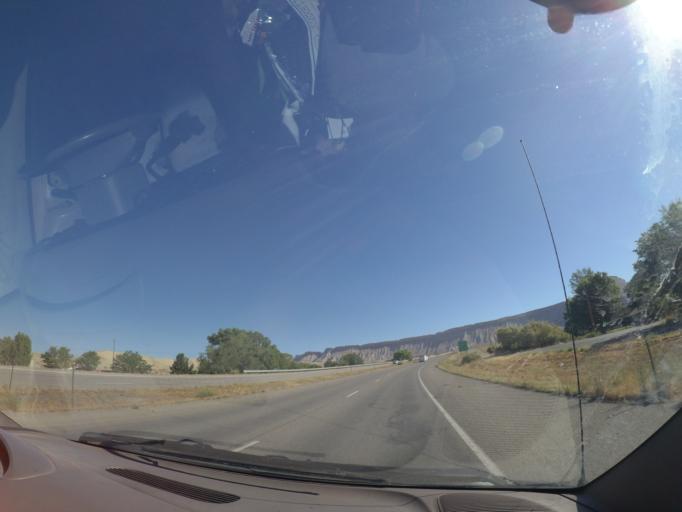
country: US
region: Colorado
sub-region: Mesa County
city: Clifton
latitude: 39.0983
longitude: -108.4484
